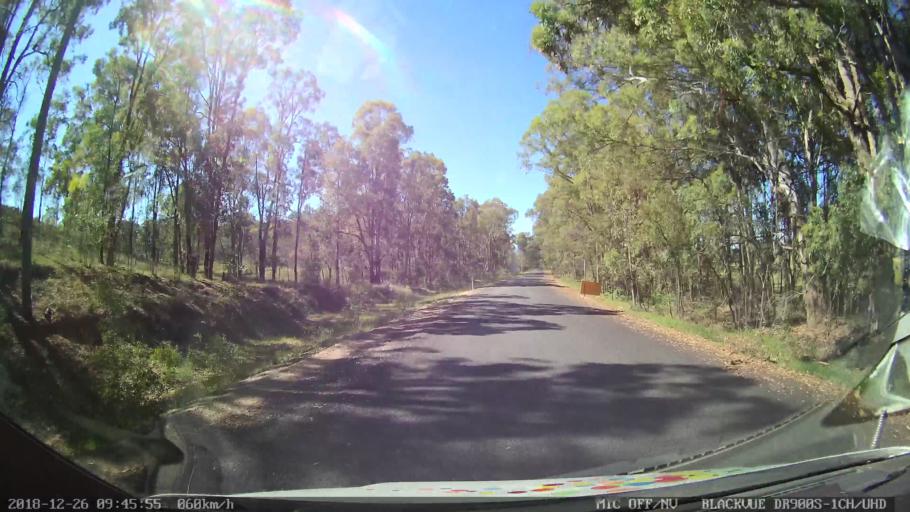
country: AU
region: New South Wales
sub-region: Mid-Western Regional
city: Kandos
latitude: -32.9650
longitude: 150.1061
